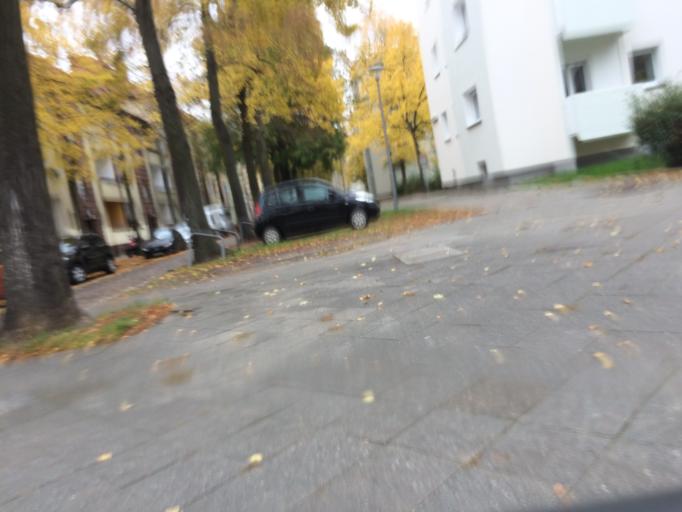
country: DE
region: Berlin
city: Wilhelmsruh
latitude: 52.5721
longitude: 13.3723
